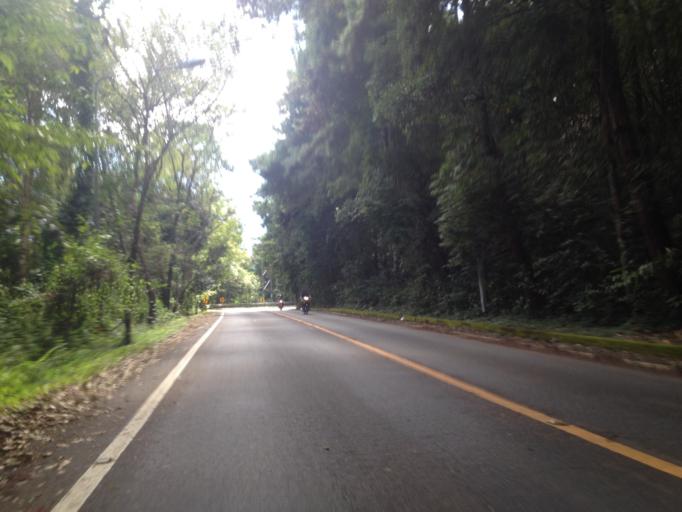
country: TH
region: Chiang Mai
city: Chiang Mai
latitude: 18.8025
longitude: 98.9054
